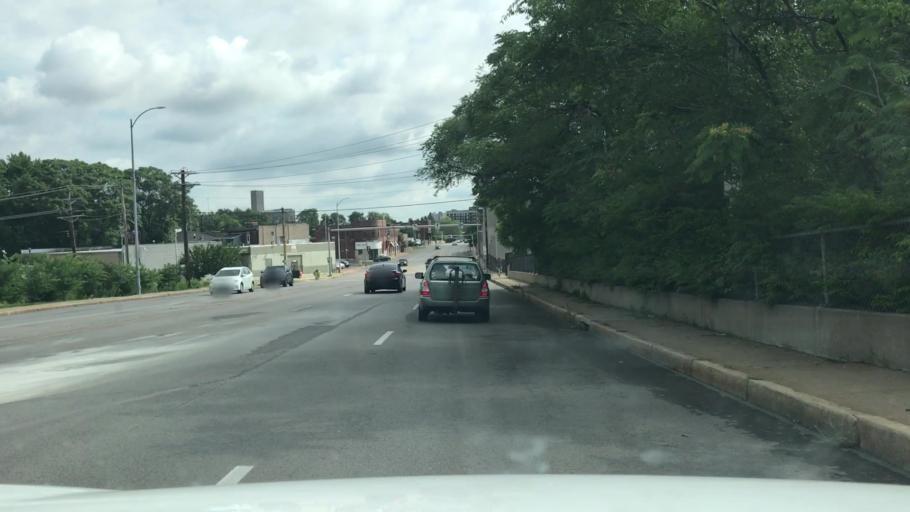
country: US
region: Missouri
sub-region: City of Saint Louis
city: St. Louis
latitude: 38.6229
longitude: -90.2549
